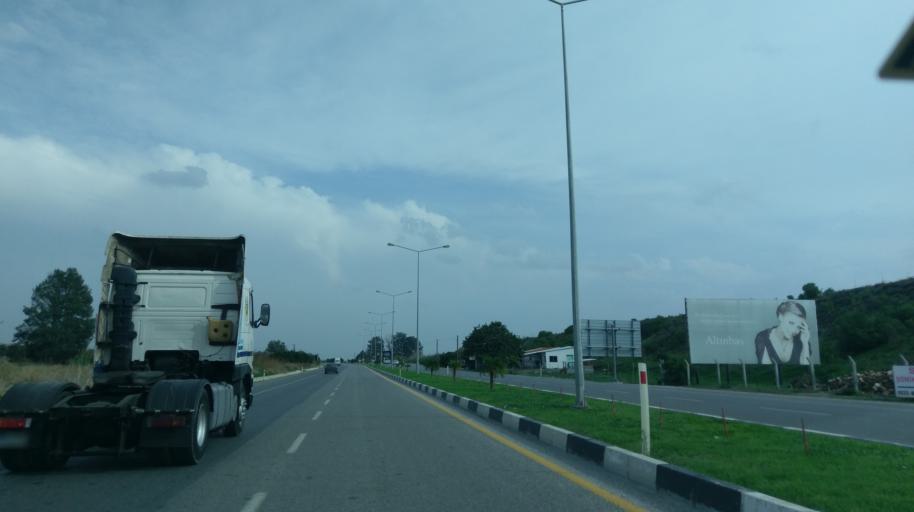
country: CY
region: Lefkosia
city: Morfou
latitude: 35.1970
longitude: 33.0088
